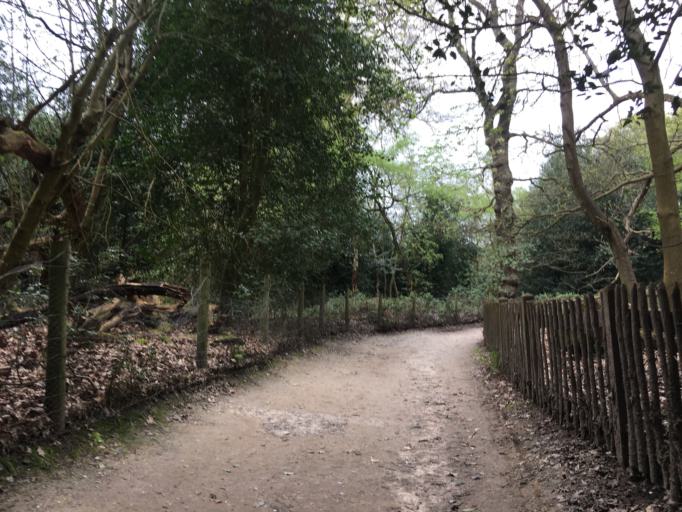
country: GB
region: England
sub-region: Greater London
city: Belsize Park
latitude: 51.5663
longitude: -0.1698
